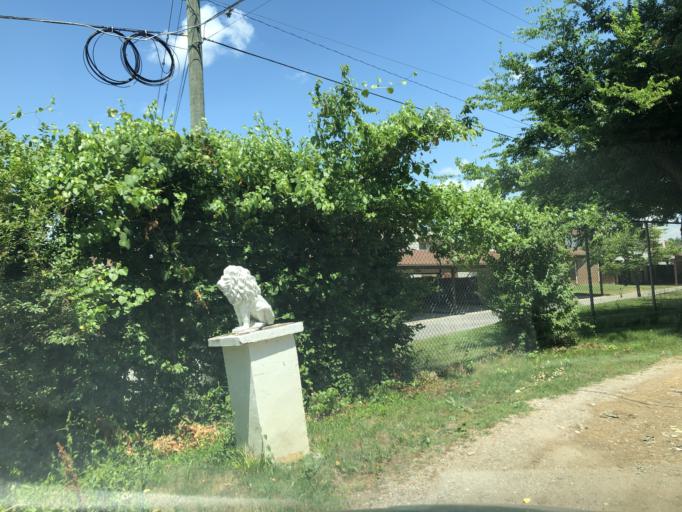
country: US
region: Tennessee
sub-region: Davidson County
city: Goodlettsville
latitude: 36.2682
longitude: -86.7212
